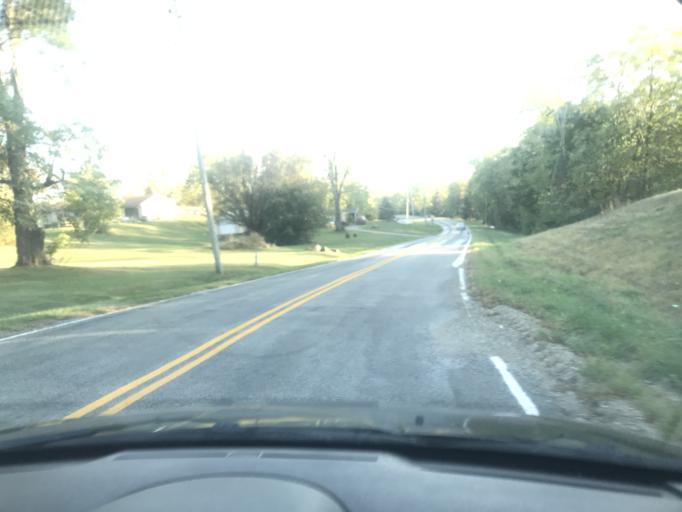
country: US
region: Ohio
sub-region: Logan County
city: De Graff
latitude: 40.2501
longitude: -83.8663
